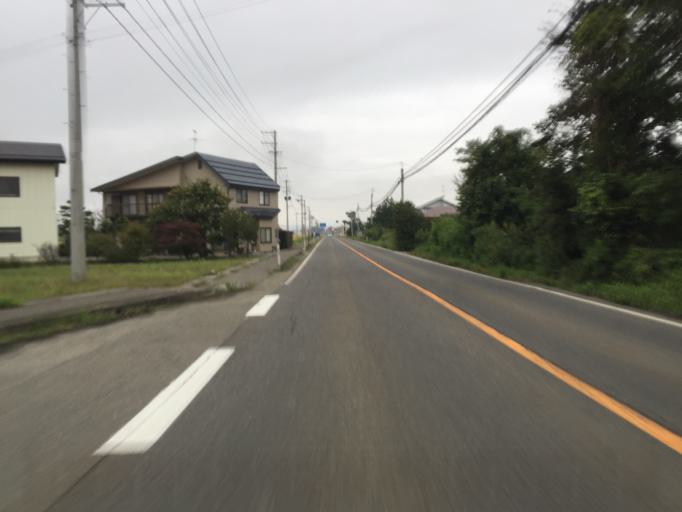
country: JP
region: Fukushima
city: Kitakata
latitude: 37.5225
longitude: 139.8943
